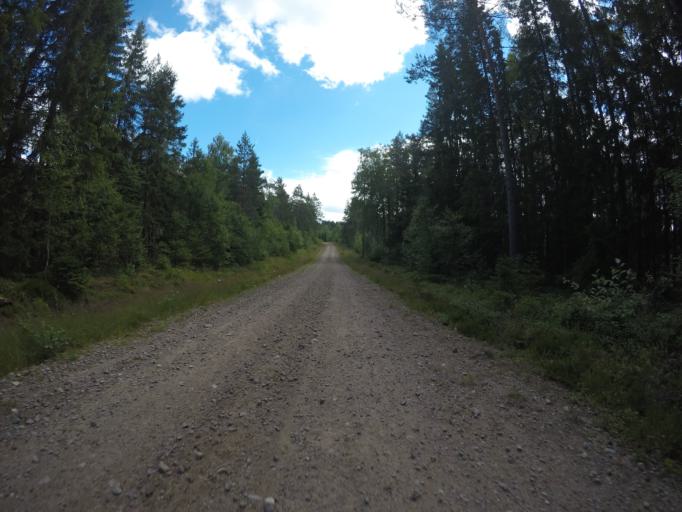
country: SE
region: Vaermland
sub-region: Filipstads Kommun
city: Lesjofors
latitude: 60.0717
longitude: 14.4531
